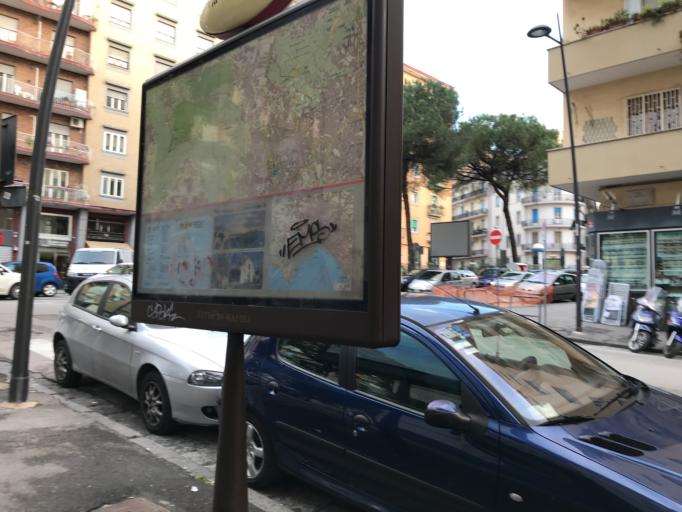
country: IT
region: Campania
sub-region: Provincia di Napoli
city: Napoli
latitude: 40.8503
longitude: 14.2276
